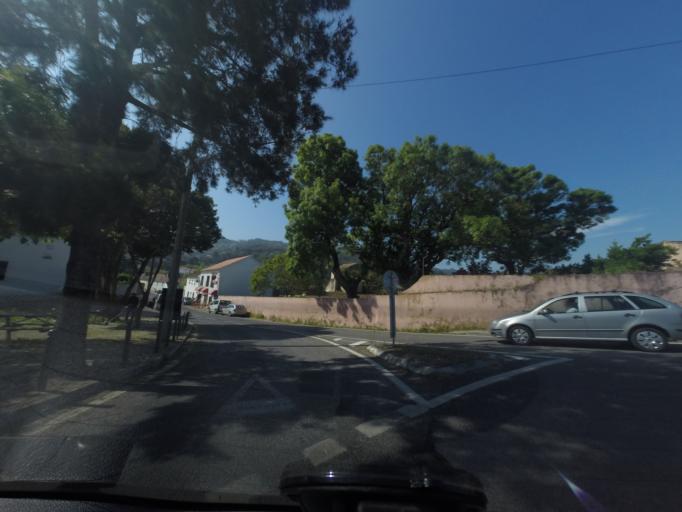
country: PT
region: Lisbon
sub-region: Sintra
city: Sintra
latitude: 38.8071
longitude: -9.3979
